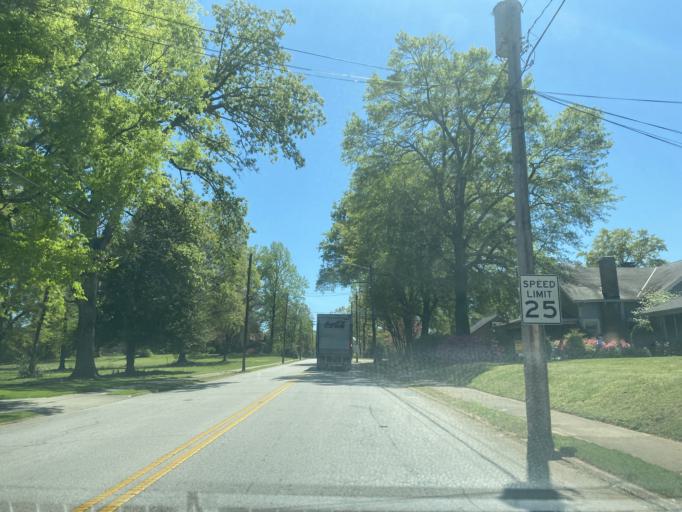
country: US
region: South Carolina
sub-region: Cherokee County
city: Gaffney
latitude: 35.0637
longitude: -81.6473
